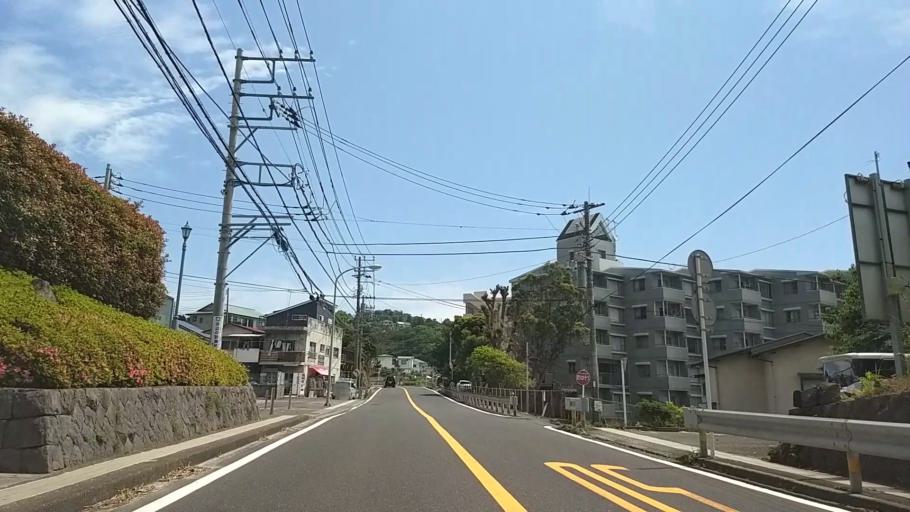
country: JP
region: Kanagawa
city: Yugawara
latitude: 35.1507
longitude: 139.1270
